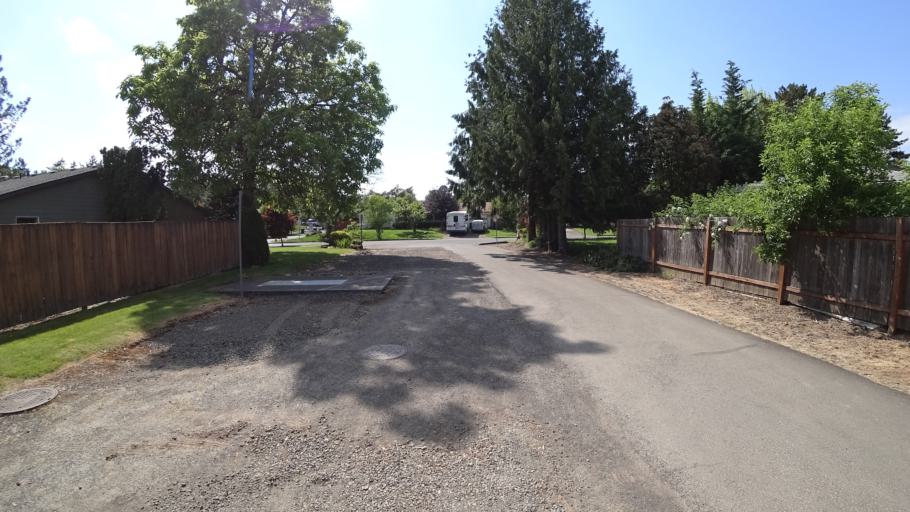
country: US
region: Oregon
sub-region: Washington County
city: Beaverton
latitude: 45.4665
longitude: -122.7909
